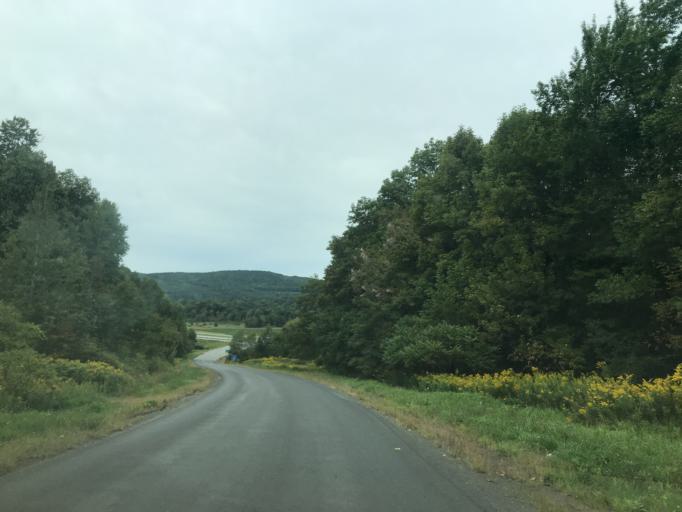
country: US
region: New York
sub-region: Otsego County
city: Worcester
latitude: 42.5907
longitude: -74.7225
